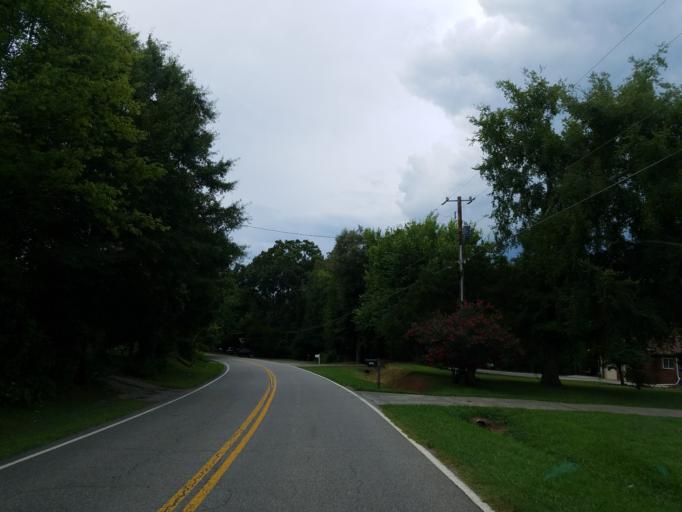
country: US
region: Georgia
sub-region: Bartow County
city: Cartersville
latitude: 34.2519
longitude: -84.8525
